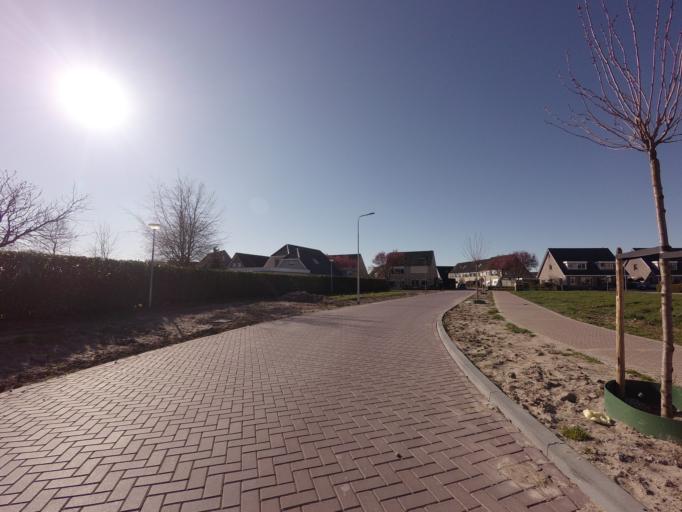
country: NL
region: Utrecht
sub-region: Gemeente Utrechtse Heuvelrug
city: Leersum
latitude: 51.9588
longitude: 5.4256
